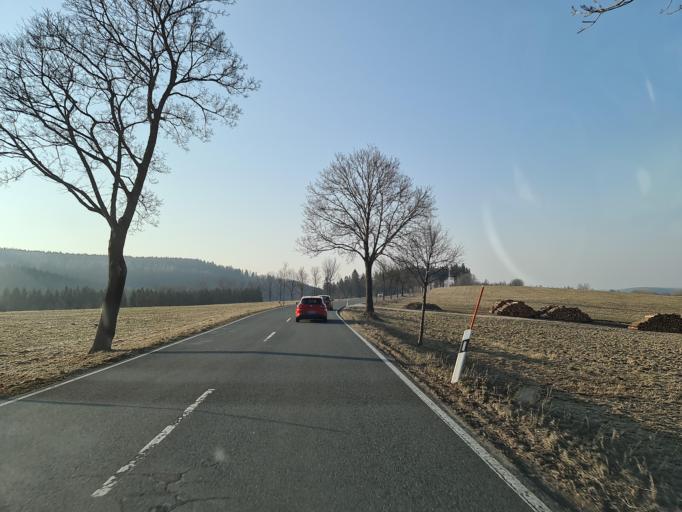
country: DE
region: Saxony
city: Eibenstock
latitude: 50.4781
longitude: 12.6121
